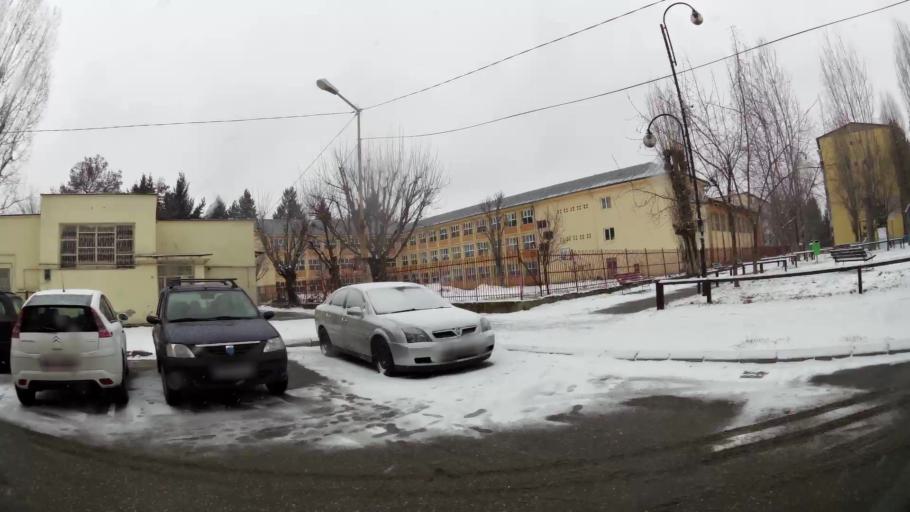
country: RO
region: Dambovita
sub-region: Municipiul Targoviste
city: Targoviste
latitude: 44.9206
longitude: 25.4703
